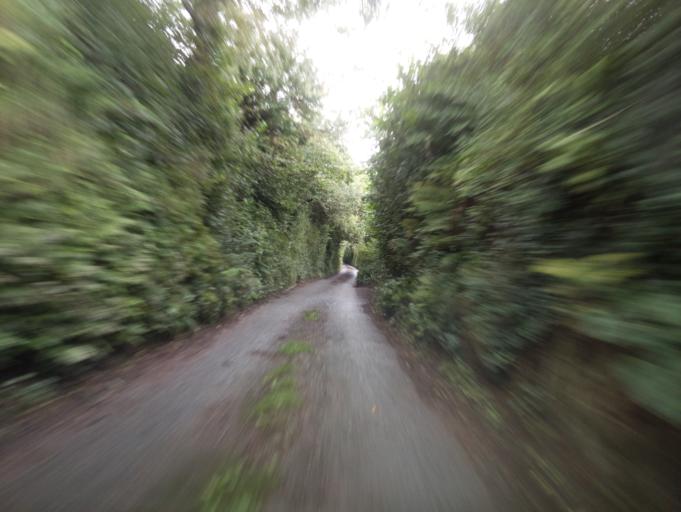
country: GB
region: England
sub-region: Devon
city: Kingsbridge
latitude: 50.2901
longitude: -3.7182
